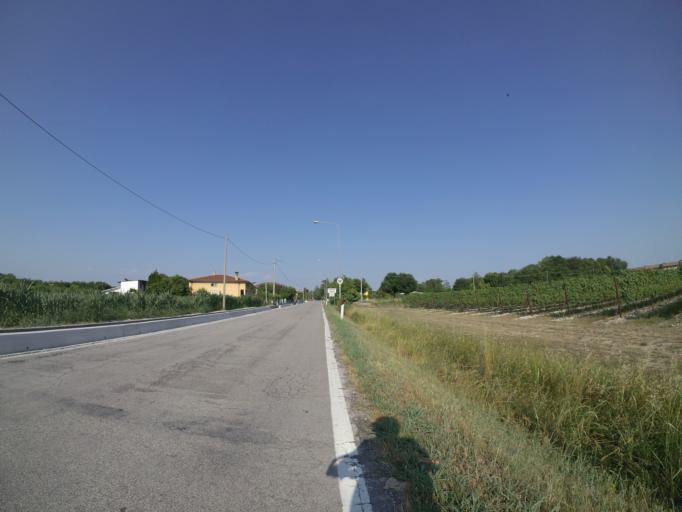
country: IT
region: Friuli Venezia Giulia
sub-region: Provincia di Udine
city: Codroipo
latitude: 45.9594
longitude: 12.9588
